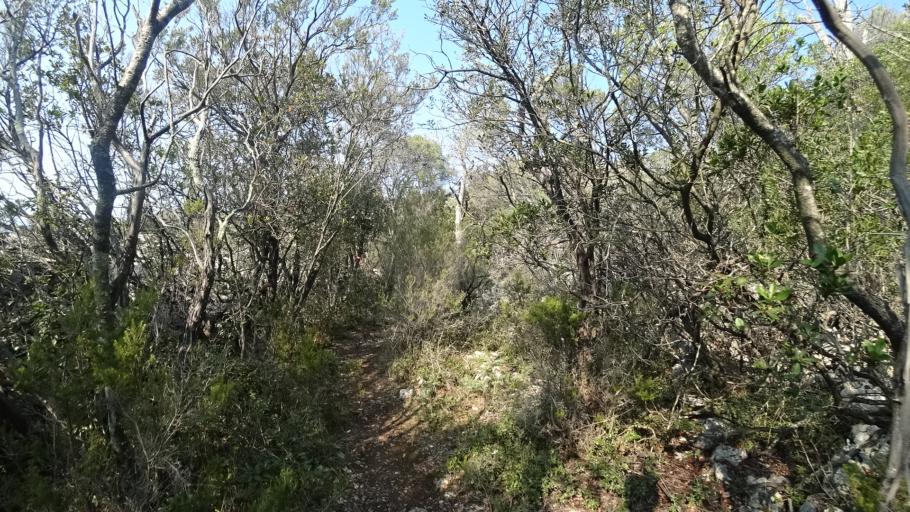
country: HR
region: Primorsko-Goranska
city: Mali Losinj
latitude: 44.4788
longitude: 14.5144
